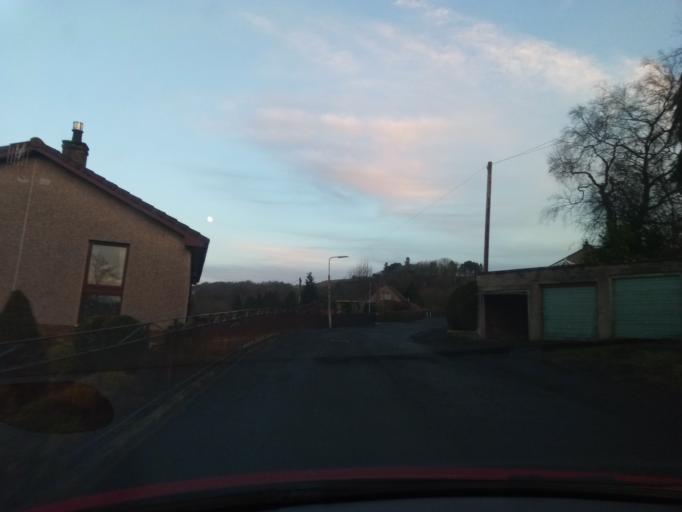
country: GB
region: Scotland
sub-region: The Scottish Borders
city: Hawick
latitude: 55.4286
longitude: -2.7717
